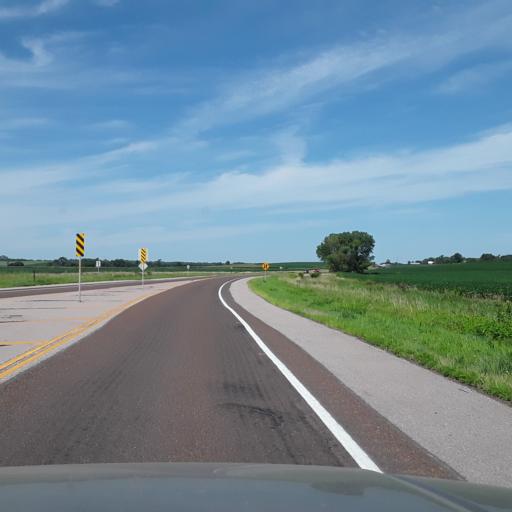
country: US
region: Nebraska
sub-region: Lancaster County
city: Lincoln
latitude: 40.8871
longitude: -96.8065
